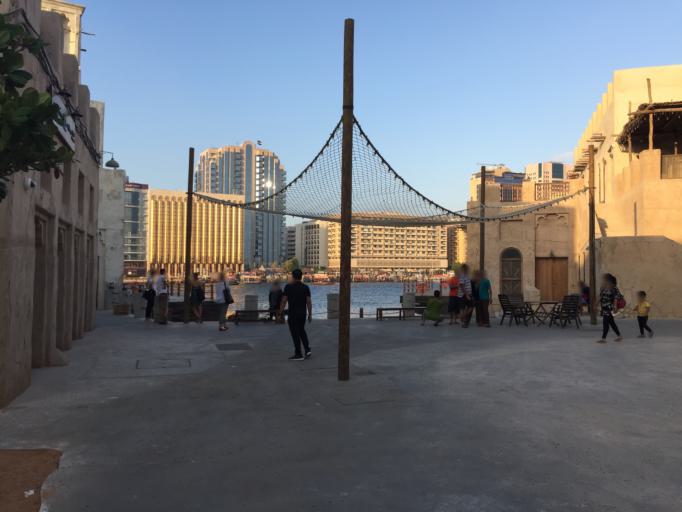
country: AE
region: Ash Shariqah
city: Sharjah
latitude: 25.2652
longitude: 55.3020
